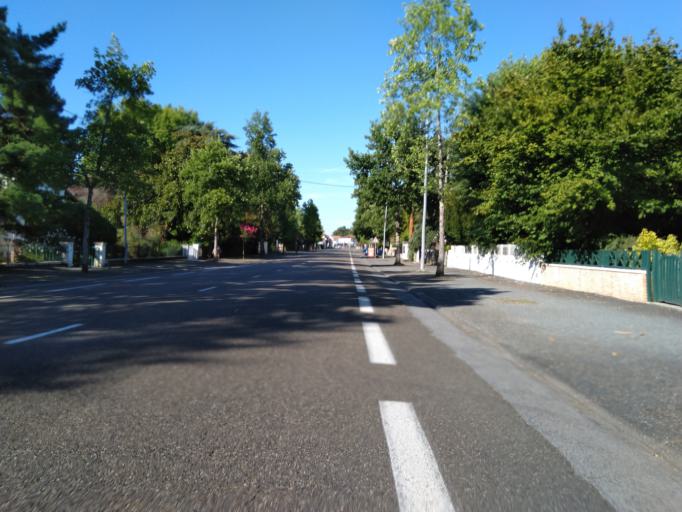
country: FR
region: Aquitaine
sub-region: Departement des Landes
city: Saint-Paul-les-Dax
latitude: 43.7256
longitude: -1.0473
